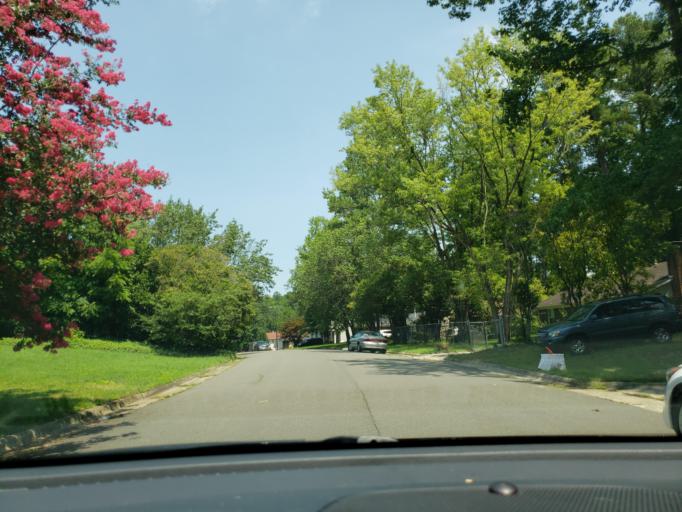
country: US
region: North Carolina
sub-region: Durham County
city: Durham
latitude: 35.9532
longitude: -78.9350
